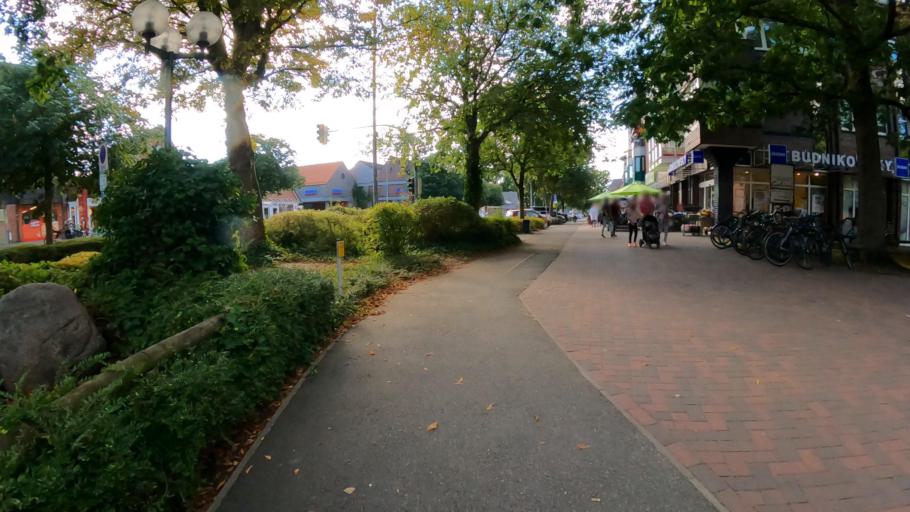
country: DE
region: Schleswig-Holstein
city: Grosshansdorf
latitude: 53.6622
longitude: 10.2862
